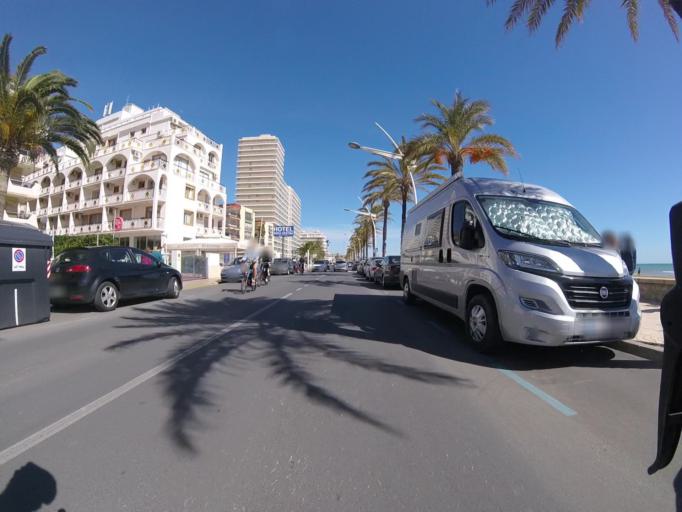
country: ES
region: Valencia
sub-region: Provincia de Castello
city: Peniscola
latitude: 40.3644
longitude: 0.4030
